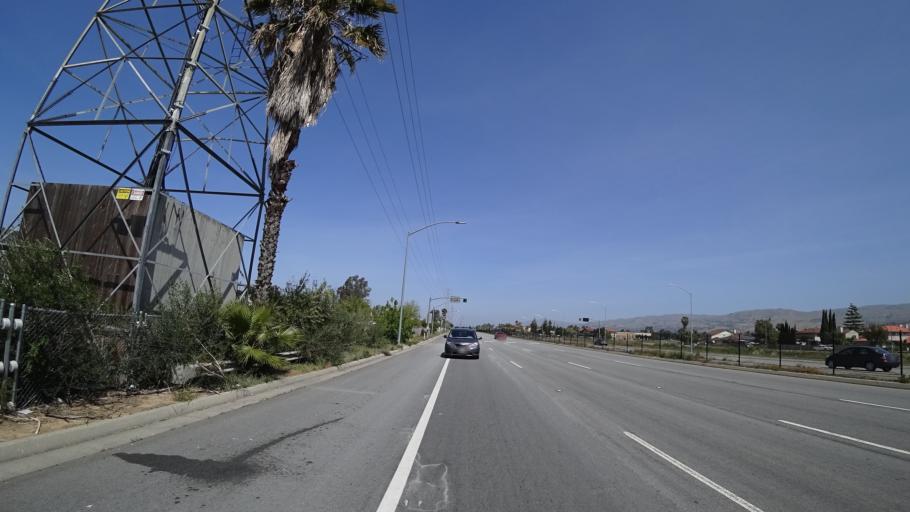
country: US
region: California
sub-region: Santa Clara County
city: Alum Rock
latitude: 37.3275
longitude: -121.8104
